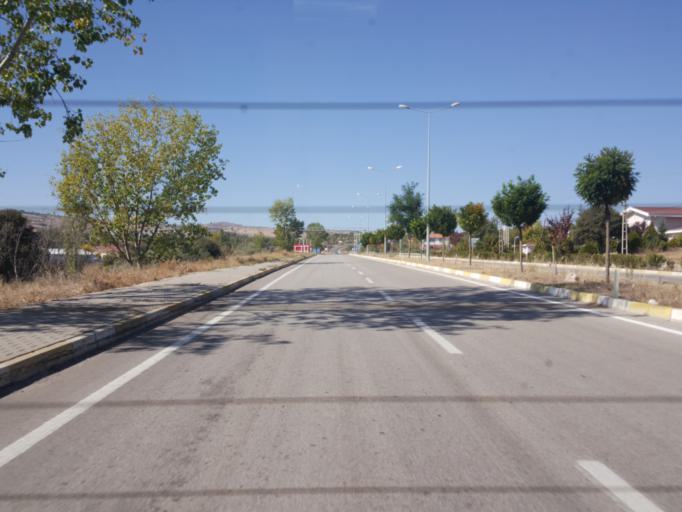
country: TR
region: Tokat
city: Zile
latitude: 40.2791
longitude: 35.8519
